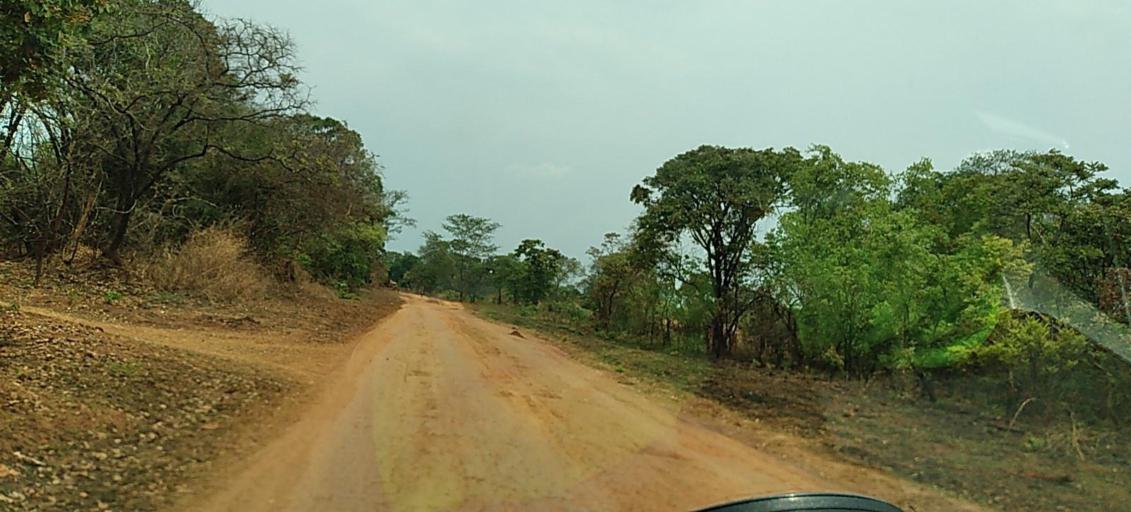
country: ZM
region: North-Western
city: Solwezi
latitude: -12.7991
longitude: 26.5345
